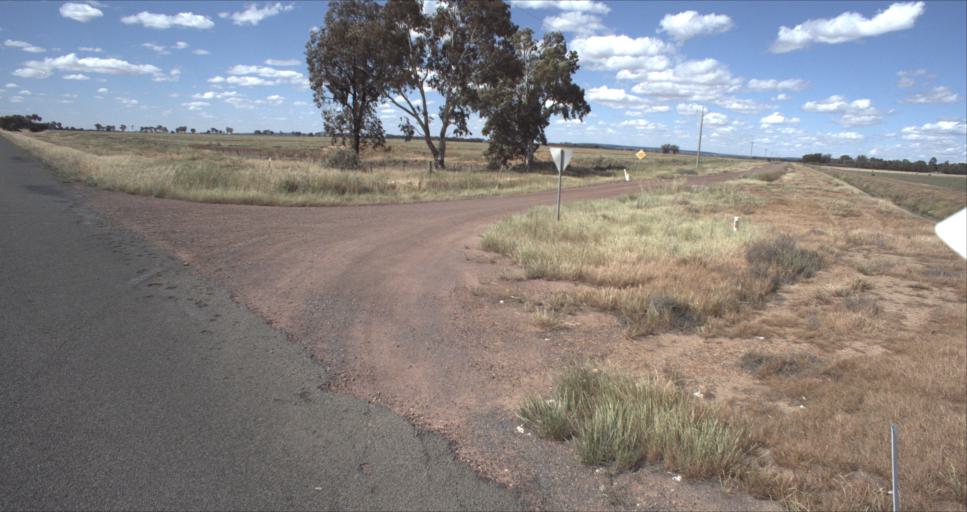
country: AU
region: New South Wales
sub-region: Leeton
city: Leeton
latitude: -34.4713
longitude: 146.2509
